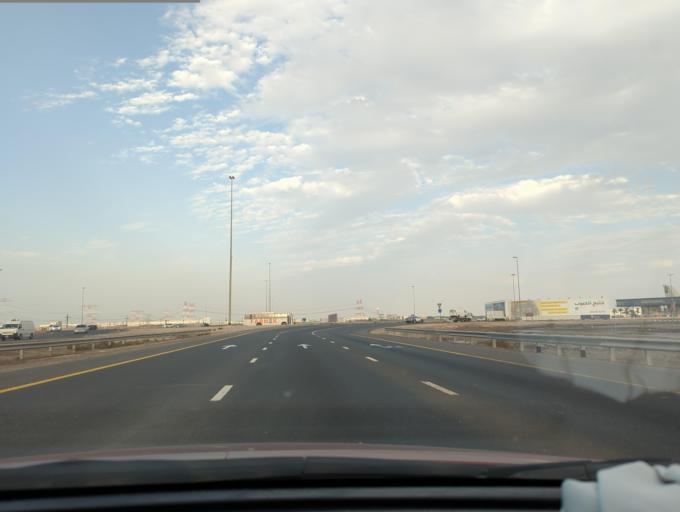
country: AE
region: Dubai
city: Dubai
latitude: 24.9092
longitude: 55.0859
